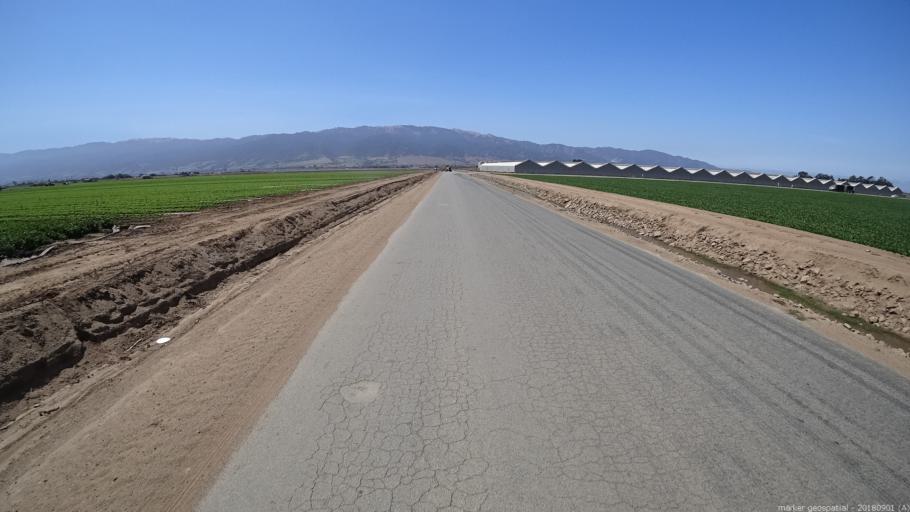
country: US
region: California
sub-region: Monterey County
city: Chualar
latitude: 36.5917
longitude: -121.5328
